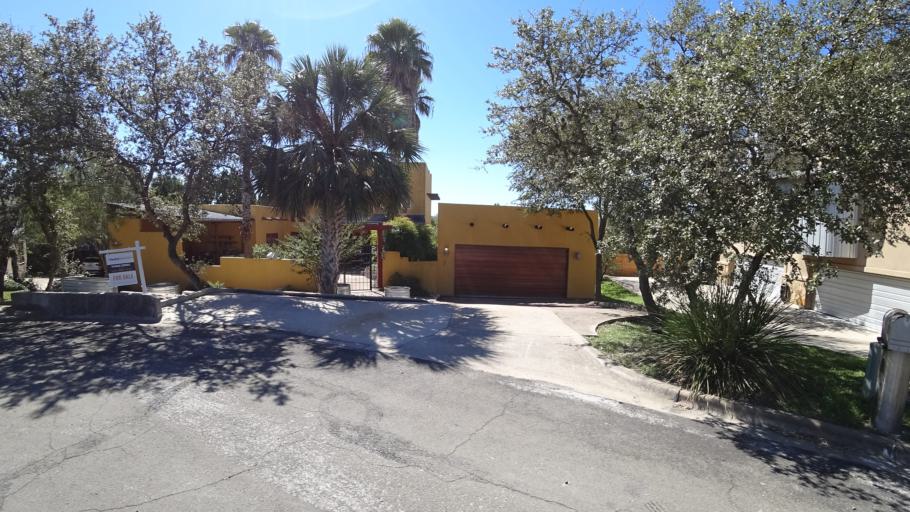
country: US
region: Texas
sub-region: Travis County
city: West Lake Hills
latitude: 30.3422
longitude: -97.7819
